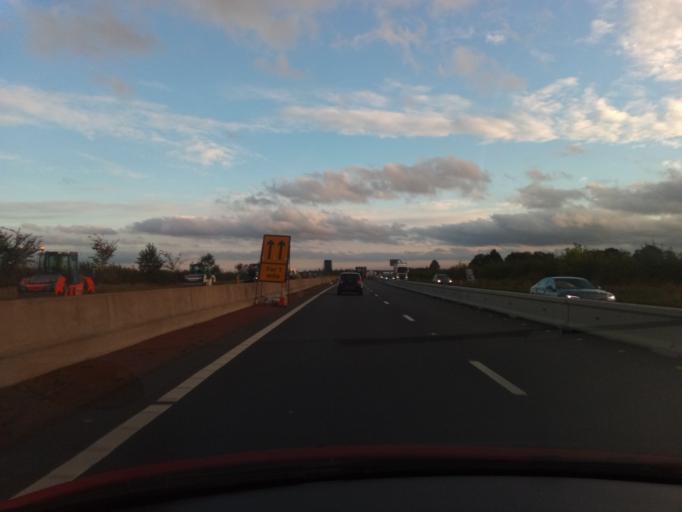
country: GB
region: England
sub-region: North Yorkshire
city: Bedale
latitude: 54.2458
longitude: -1.5031
